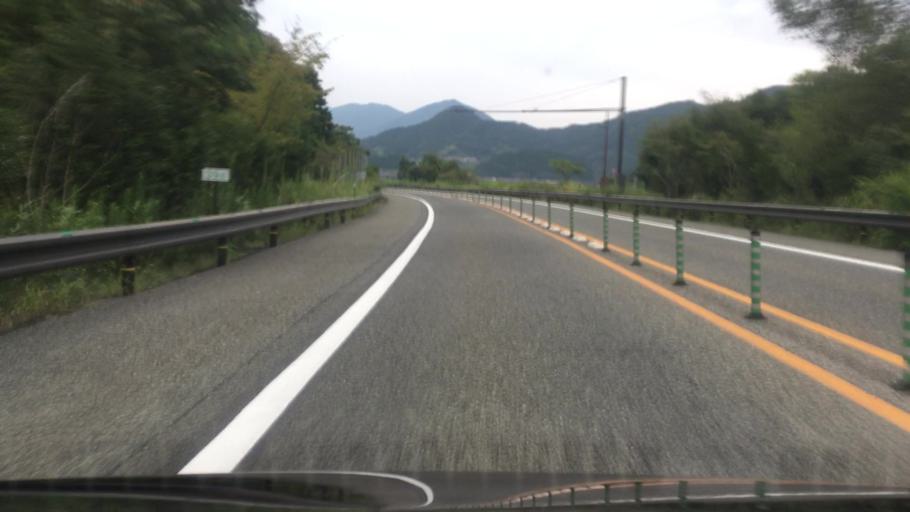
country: JP
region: Kyoto
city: Fukuchiyama
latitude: 35.3050
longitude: 134.8926
